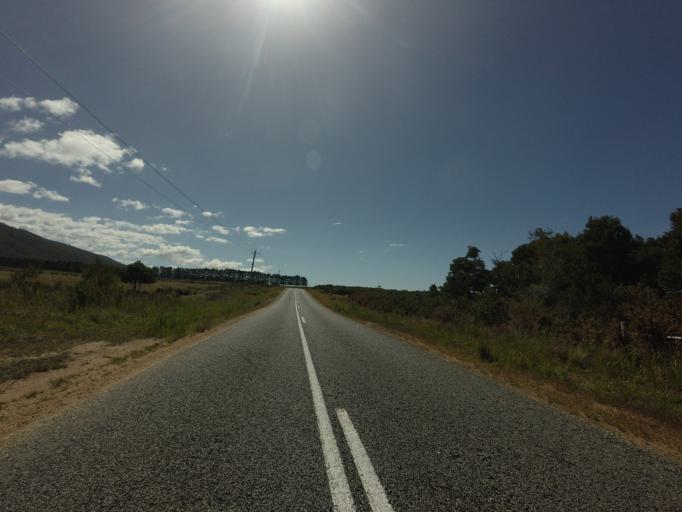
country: AU
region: Tasmania
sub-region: Break O'Day
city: St Helens
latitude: -41.7594
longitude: 148.2733
